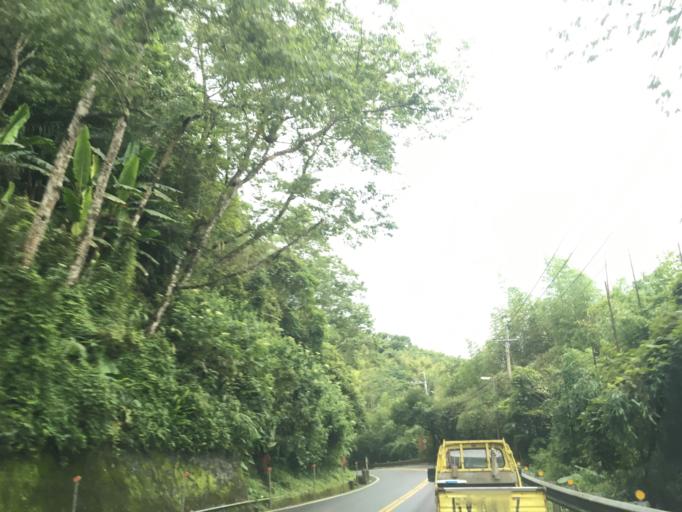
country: TW
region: Taiwan
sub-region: Chiayi
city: Jiayi Shi
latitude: 23.4622
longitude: 120.6889
